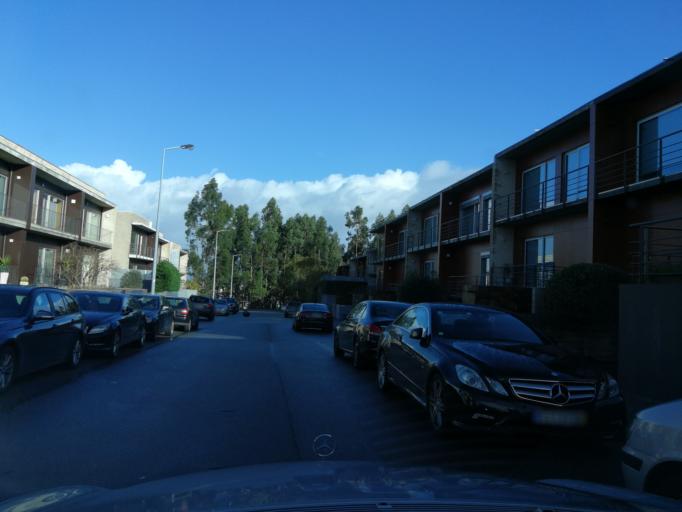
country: PT
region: Braga
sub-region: Braga
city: Braga
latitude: 41.5386
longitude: -8.3947
